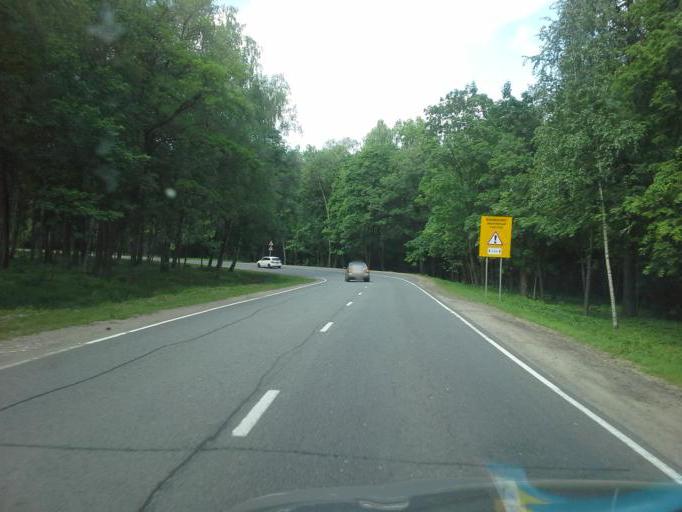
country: RU
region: Moskovskaya
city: Odintsovo
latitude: 55.6936
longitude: 37.2377
